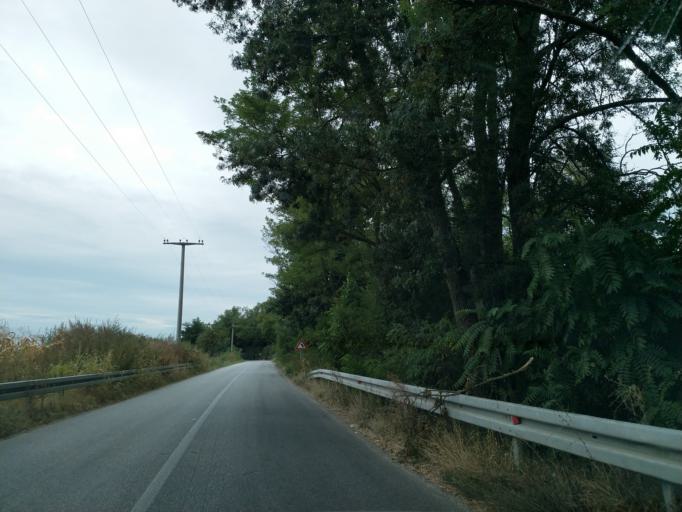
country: RS
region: Central Serbia
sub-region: Pomoravski Okrug
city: Paracin
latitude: 43.8449
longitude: 21.3766
